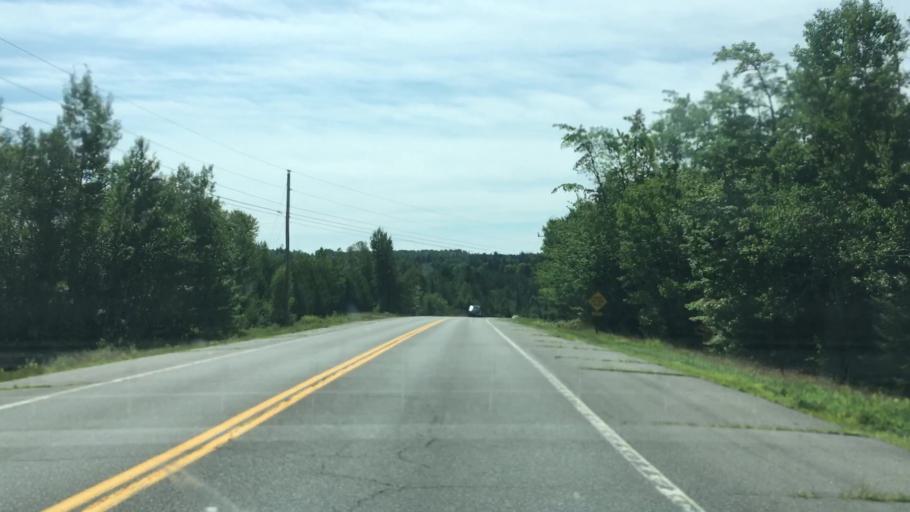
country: CA
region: New Brunswick
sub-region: Charlotte County
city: Saint Andrews
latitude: 45.0387
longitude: -67.1125
